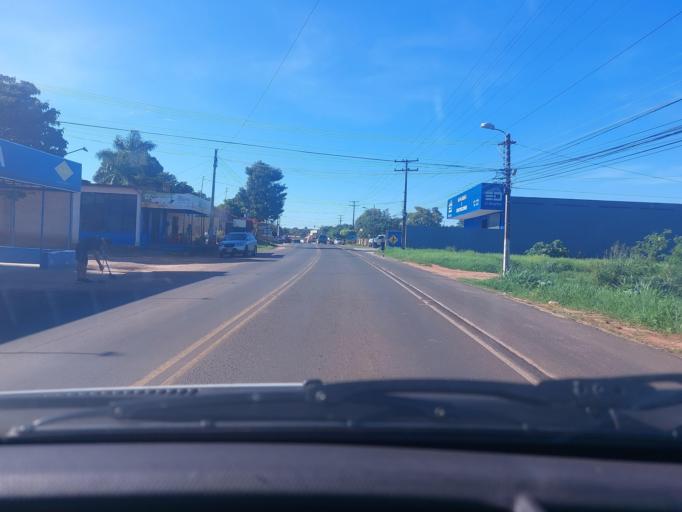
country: PY
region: San Pedro
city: Guayaybi
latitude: -24.6713
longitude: -56.4534
